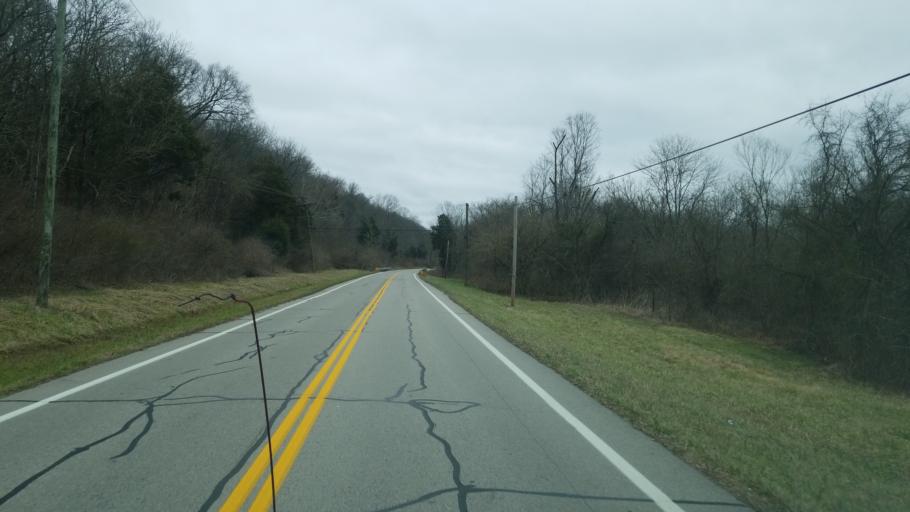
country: US
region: Kentucky
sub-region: Bracken County
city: Brooksville
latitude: 38.8013
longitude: -84.1696
